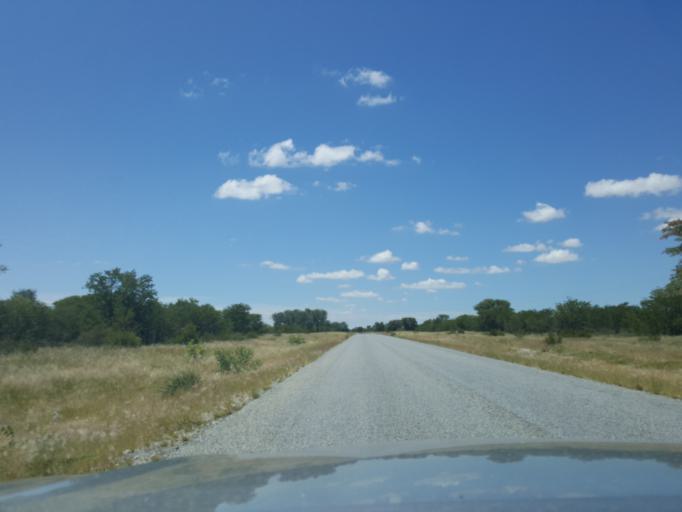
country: BW
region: Central
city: Nata
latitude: -20.1478
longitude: 25.7307
